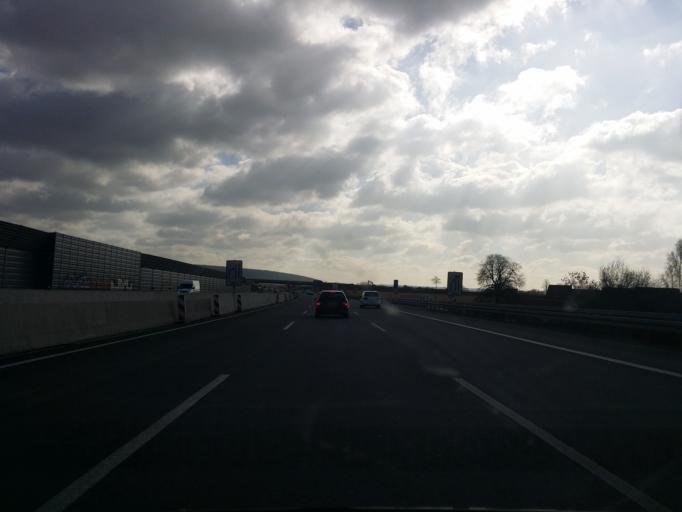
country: DE
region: Lower Saxony
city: Bockenem
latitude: 52.0033
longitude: 10.1576
